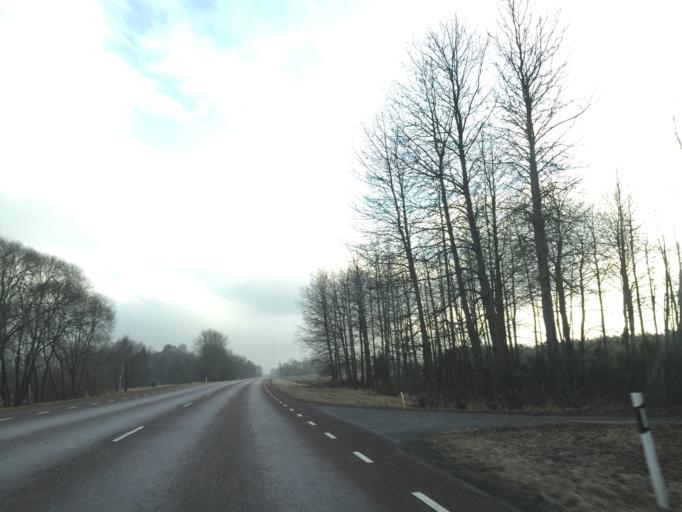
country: EE
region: Saare
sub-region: Kuressaare linn
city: Kuressaare
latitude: 58.3612
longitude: 22.7166
